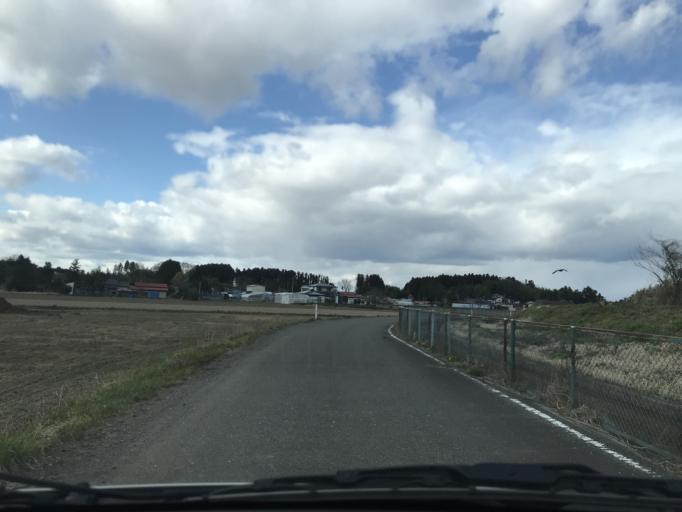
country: JP
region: Miyagi
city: Wakuya
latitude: 38.6452
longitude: 141.1996
